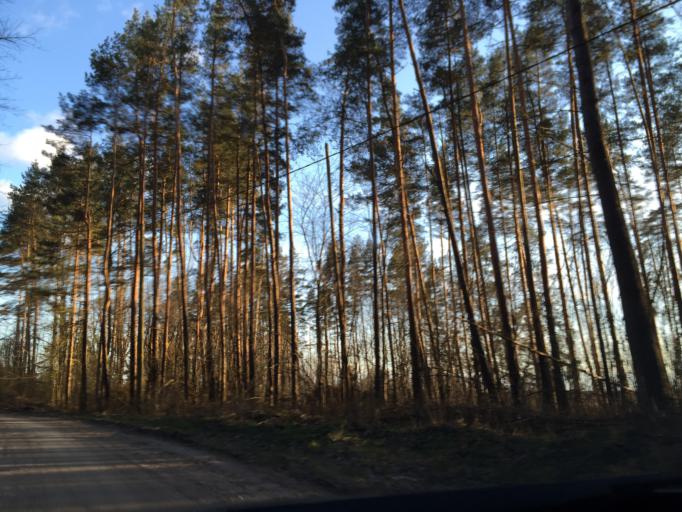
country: LV
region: Kekava
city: Kekava
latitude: 56.8523
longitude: 24.2244
